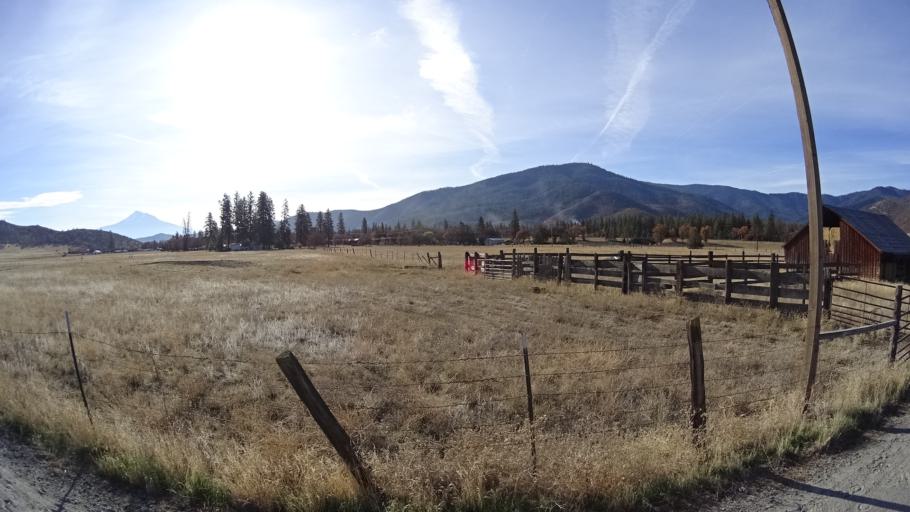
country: US
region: California
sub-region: Siskiyou County
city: Yreka
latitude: 41.6716
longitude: -122.6093
